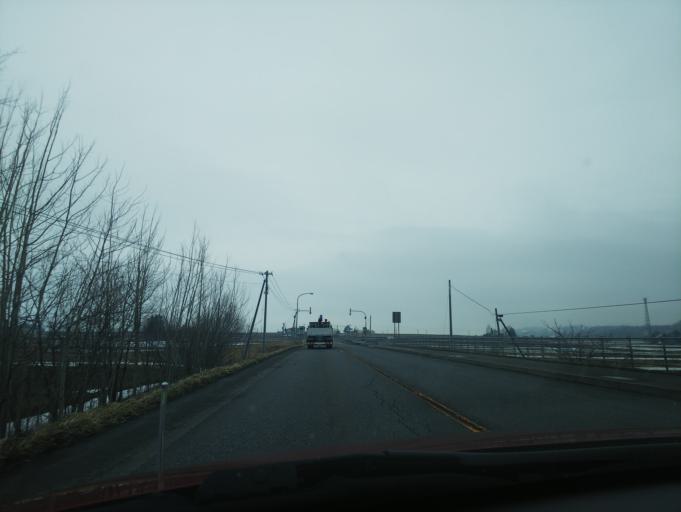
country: JP
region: Hokkaido
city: Nayoro
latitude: 44.0670
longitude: 142.3973
